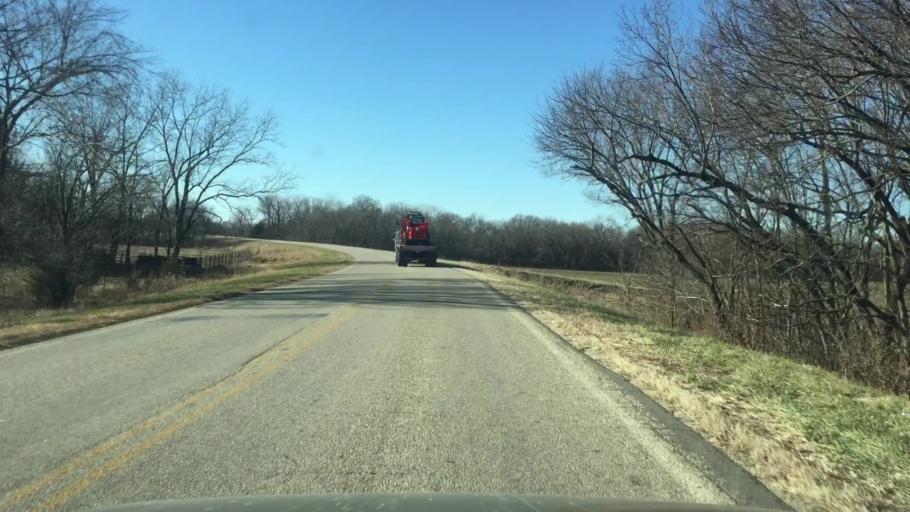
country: US
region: Kansas
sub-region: Allen County
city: Iola
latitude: 37.8847
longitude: -95.4318
